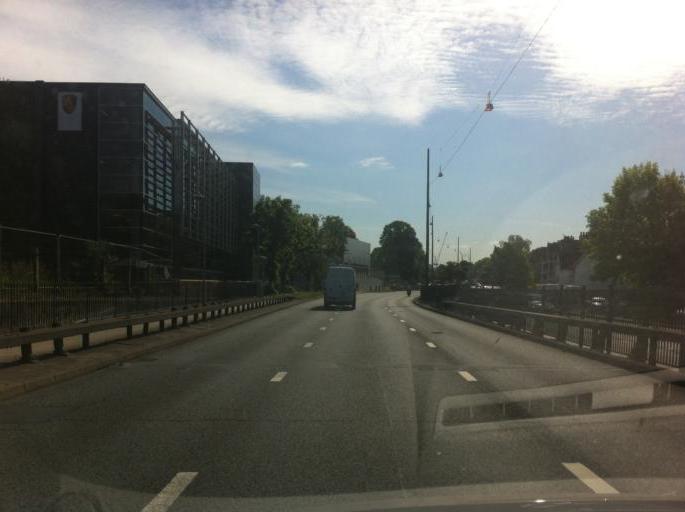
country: GB
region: England
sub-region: Greater London
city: Acton
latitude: 51.4894
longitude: -0.2770
